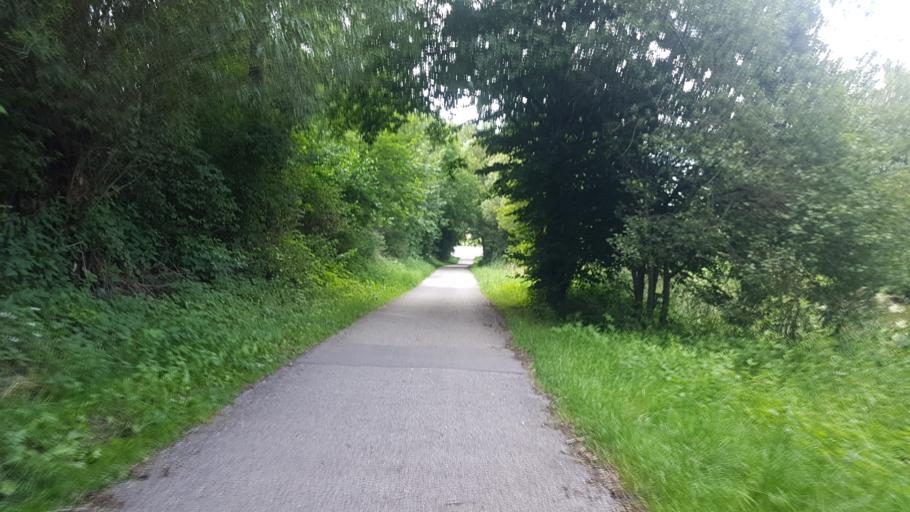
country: DE
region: Bavaria
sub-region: Regierungsbezirk Mittelfranken
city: Pappenheim
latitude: 48.9245
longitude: 10.9663
